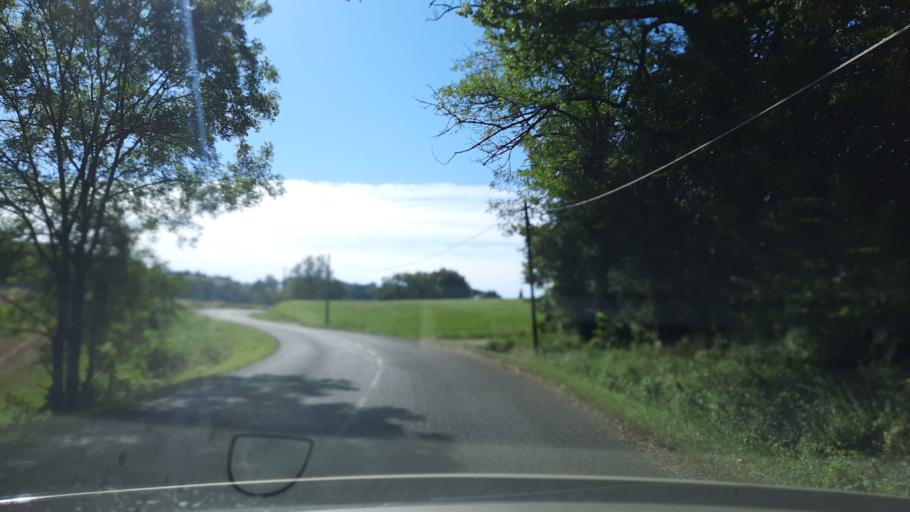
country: FR
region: Midi-Pyrenees
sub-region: Departement du Tarn-et-Garonne
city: Realville
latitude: 44.1875
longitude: 1.4597
